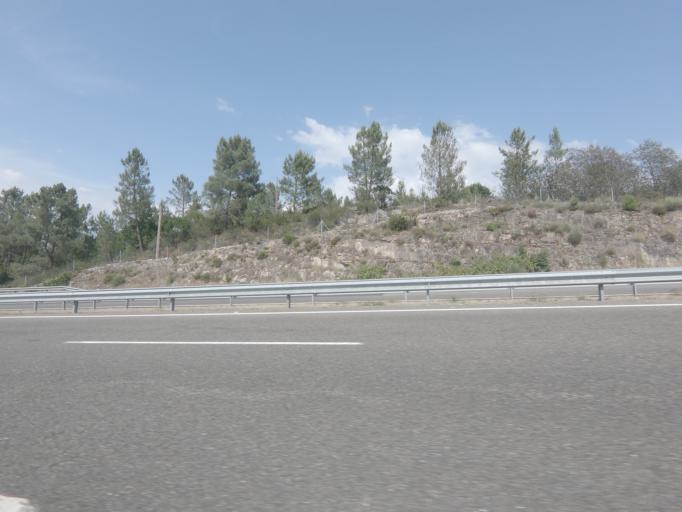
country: ES
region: Galicia
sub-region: Provincia de Ourense
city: Ourense
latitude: 42.2867
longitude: -7.8751
